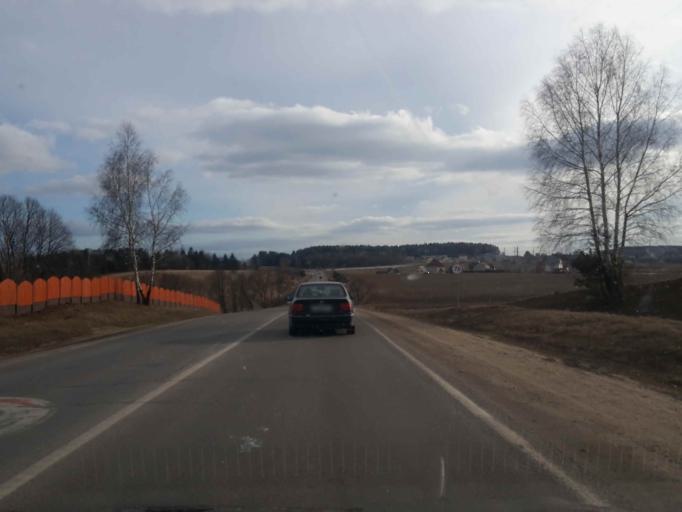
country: BY
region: Minsk
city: Bal'shavik
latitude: 54.0383
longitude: 27.5616
